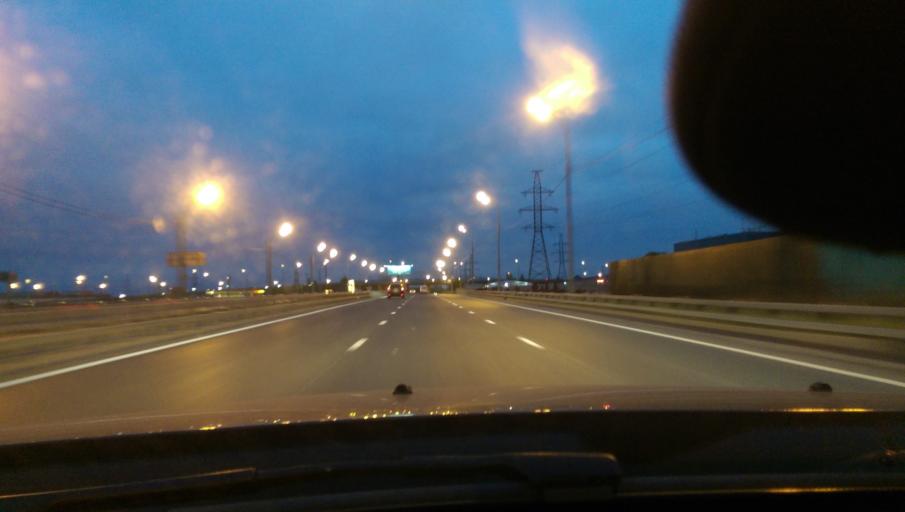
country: RU
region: Moscow
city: Vatutino
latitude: 55.9152
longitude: 37.6684
